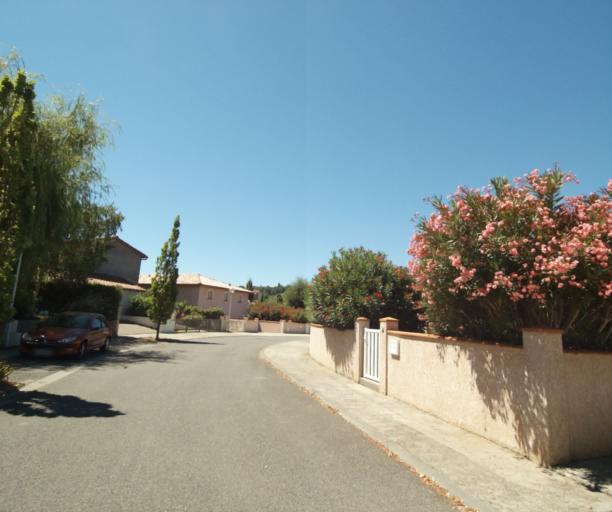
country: FR
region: Midi-Pyrenees
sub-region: Departement de la Haute-Garonne
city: Pechabou
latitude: 43.5125
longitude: 1.5126
